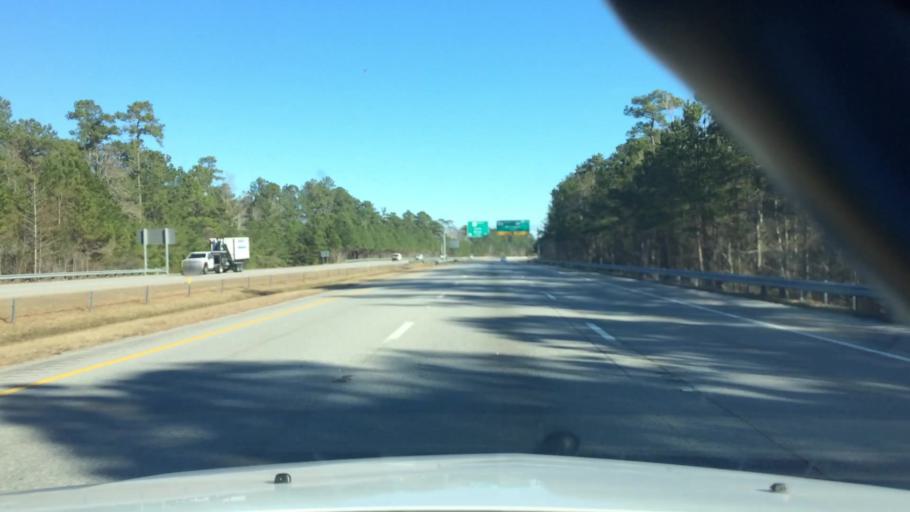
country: US
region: South Carolina
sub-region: Horry County
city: North Myrtle Beach
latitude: 33.8600
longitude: -78.6956
